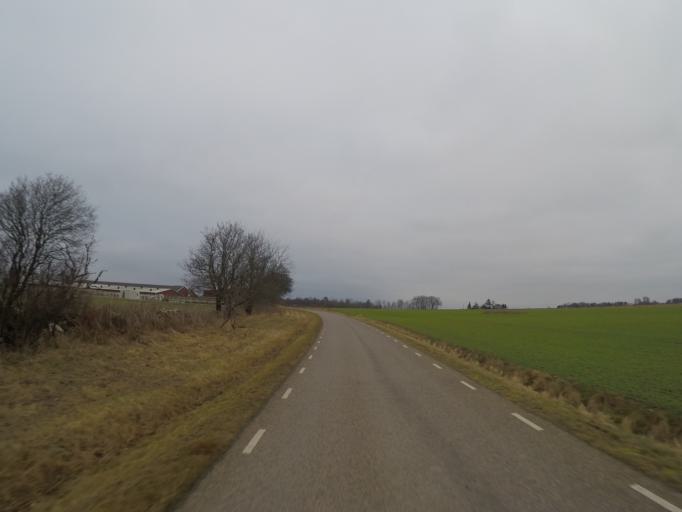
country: SE
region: Skane
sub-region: Hoors Kommun
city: Loberod
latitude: 55.7904
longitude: 13.4020
